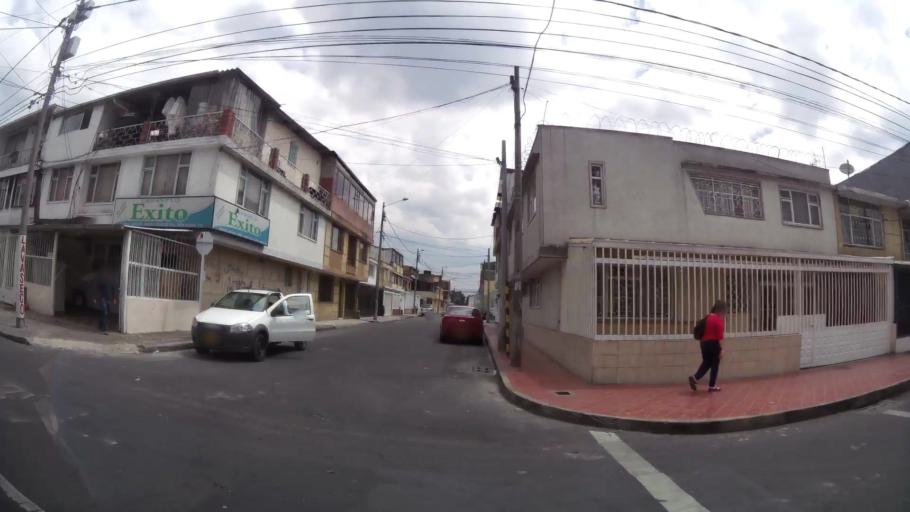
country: CO
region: Bogota D.C.
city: Bogota
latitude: 4.5979
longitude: -74.1030
